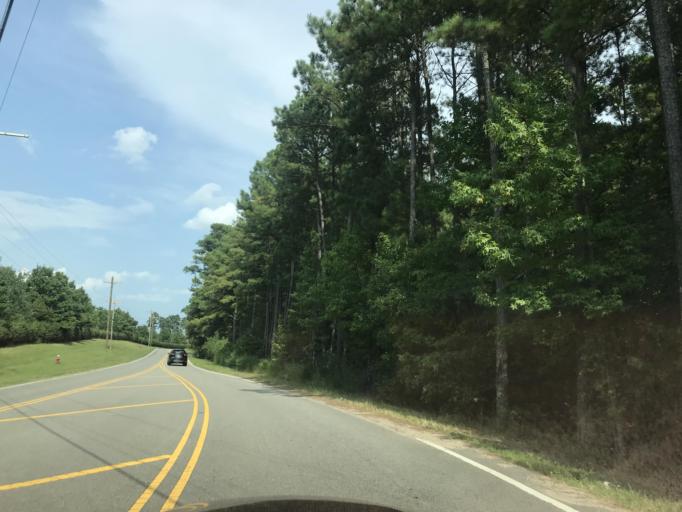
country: US
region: North Carolina
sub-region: Wake County
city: Morrisville
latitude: 35.8379
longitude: -78.8692
